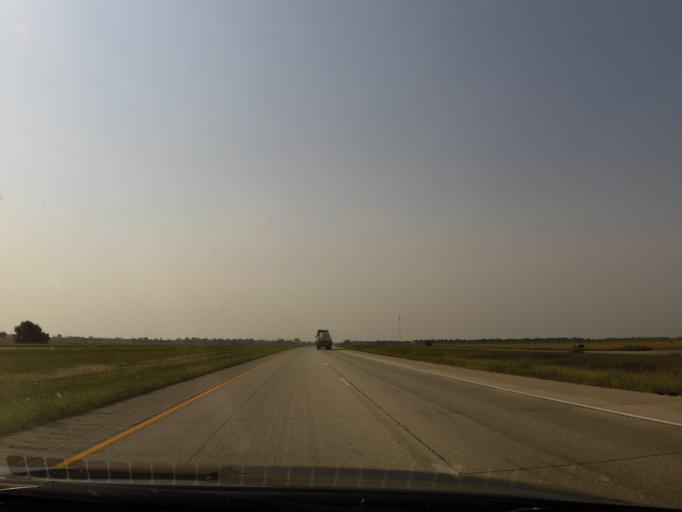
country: US
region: North Dakota
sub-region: Traill County
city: Hillsboro
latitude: 47.4334
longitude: -97.0701
